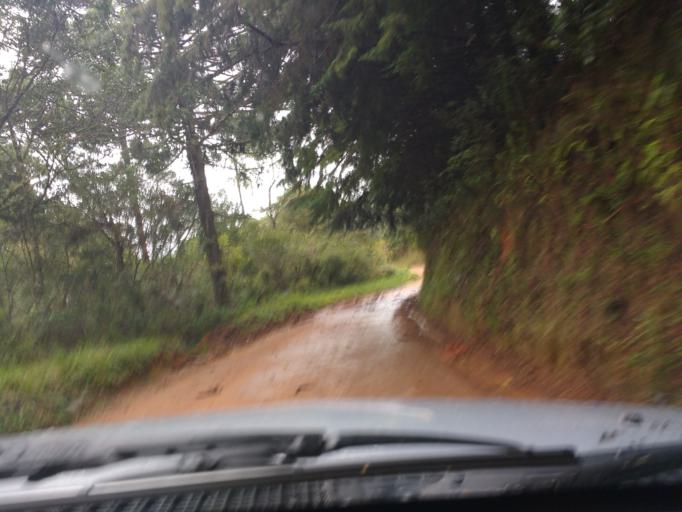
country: BR
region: Minas Gerais
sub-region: Cambui
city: Cambui
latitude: -22.7458
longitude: -45.9193
